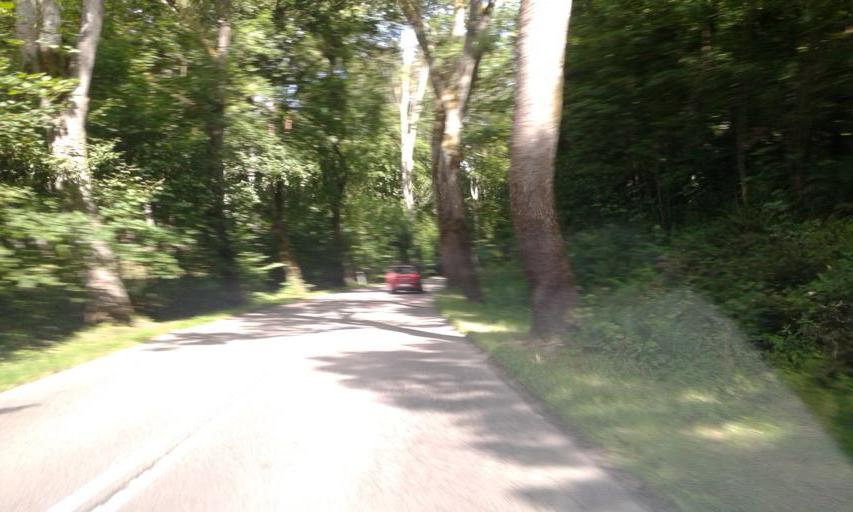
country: PL
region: West Pomeranian Voivodeship
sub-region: Powiat koszalinski
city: Polanow
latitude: 54.2251
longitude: 16.6966
